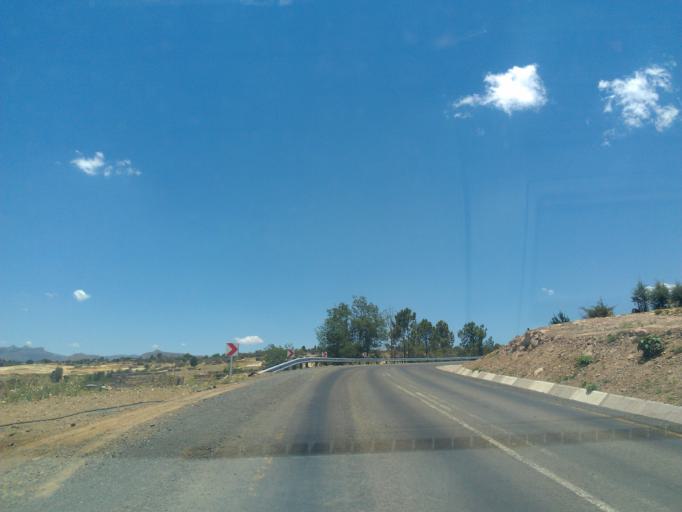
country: LS
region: Leribe
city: Maputsoe
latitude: -29.0949
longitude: 27.9621
